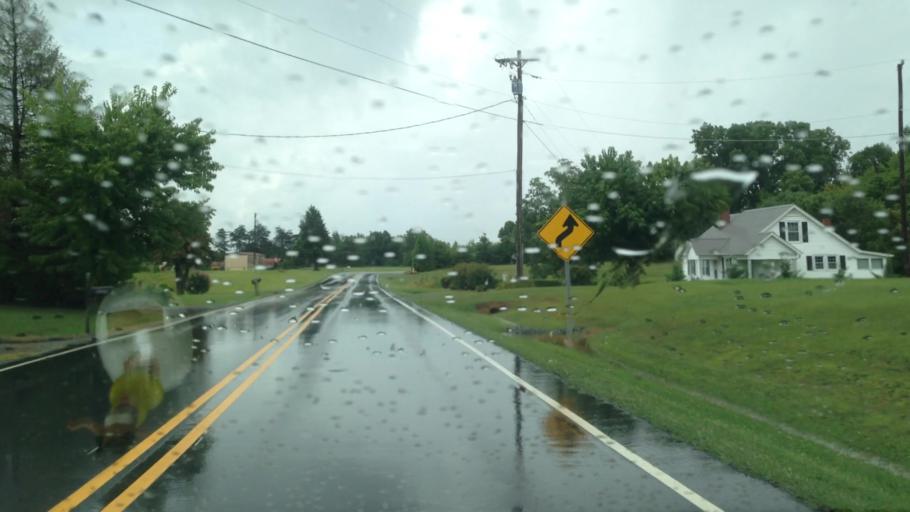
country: US
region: North Carolina
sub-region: Stokes County
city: Danbury
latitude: 36.4559
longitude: -80.0992
